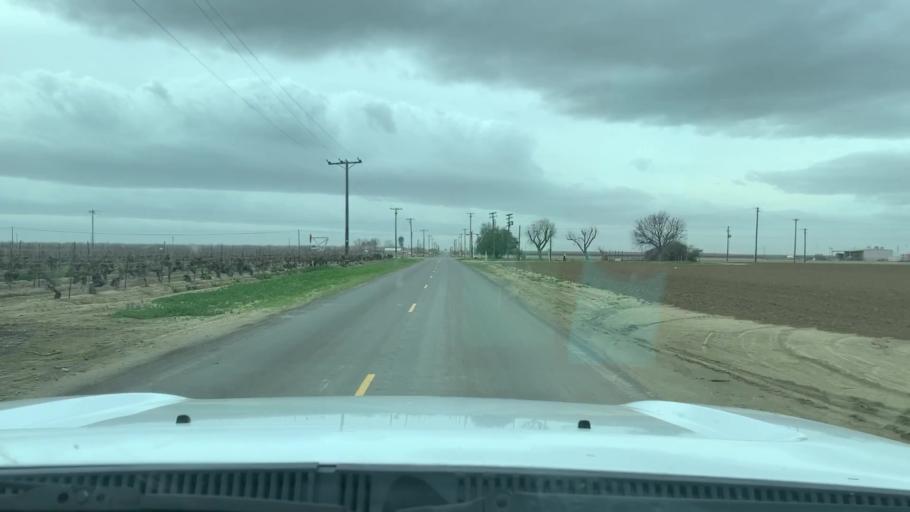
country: US
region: California
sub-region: Kern County
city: Shafter
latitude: 35.5292
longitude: -119.2756
